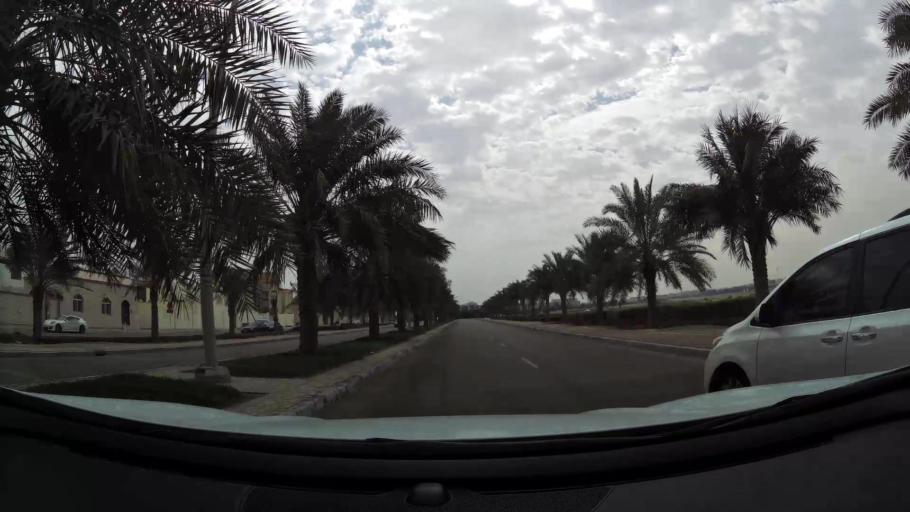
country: AE
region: Abu Dhabi
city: Abu Dhabi
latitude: 24.3169
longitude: 54.6150
